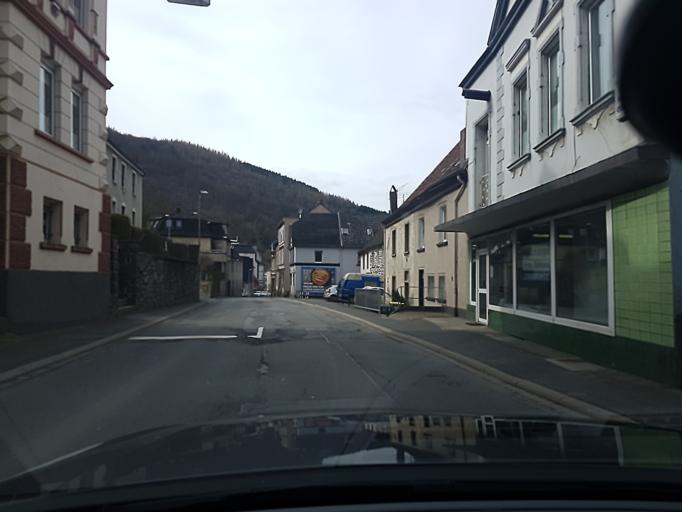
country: DE
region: North Rhine-Westphalia
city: Altena
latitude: 51.3020
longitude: 7.6757
